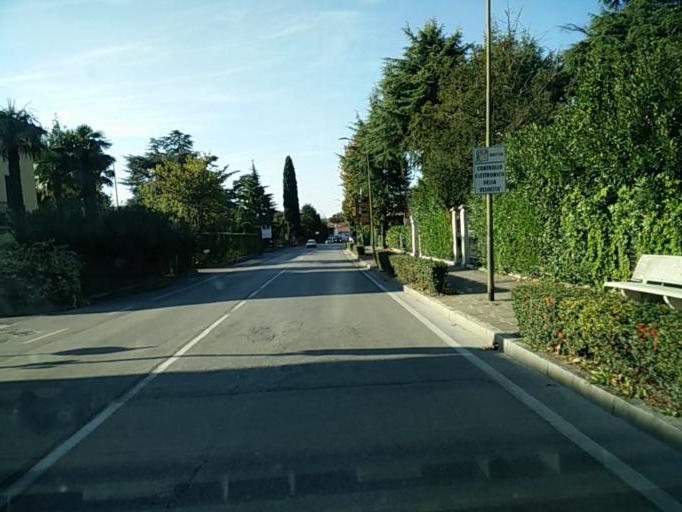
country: IT
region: Lombardy
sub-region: Provincia di Brescia
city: Desenzano del Garda
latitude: 45.4620
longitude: 10.5570
